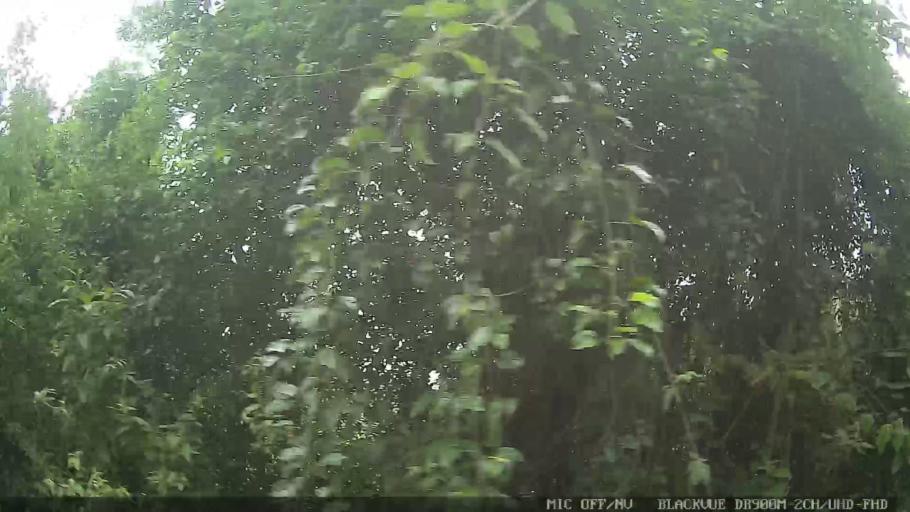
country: BR
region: Sao Paulo
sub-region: Aruja
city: Aruja
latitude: -23.3965
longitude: -46.2392
